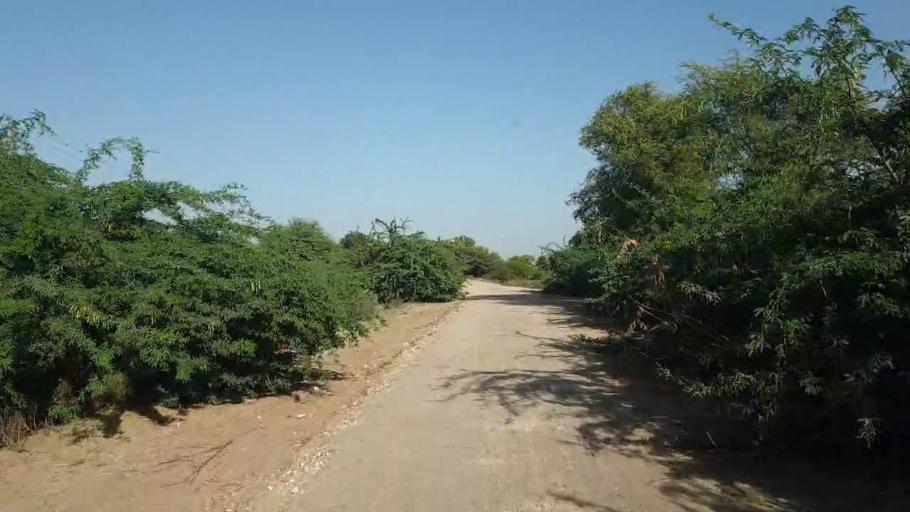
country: PK
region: Sindh
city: Badin
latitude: 24.6038
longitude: 68.9204
